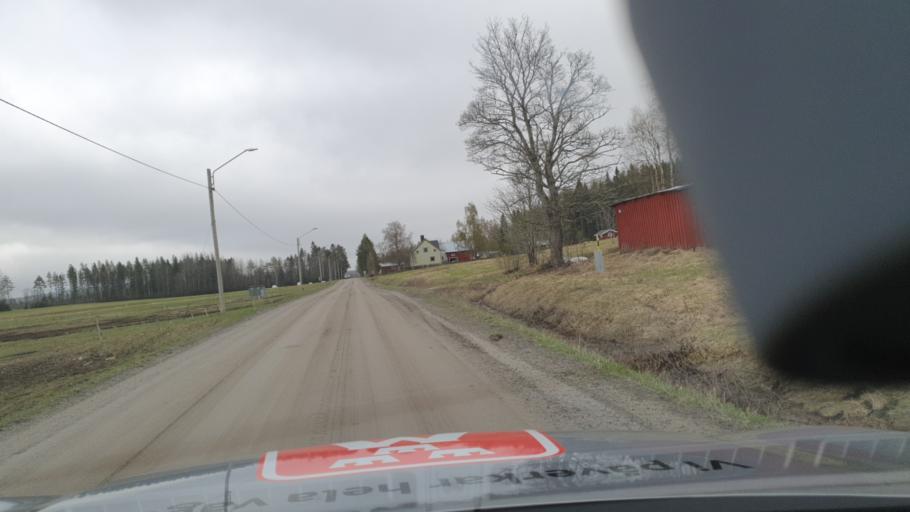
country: SE
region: Vaesterbotten
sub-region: Bjurholms Kommun
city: Bjurholm
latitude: 63.6514
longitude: 19.0447
